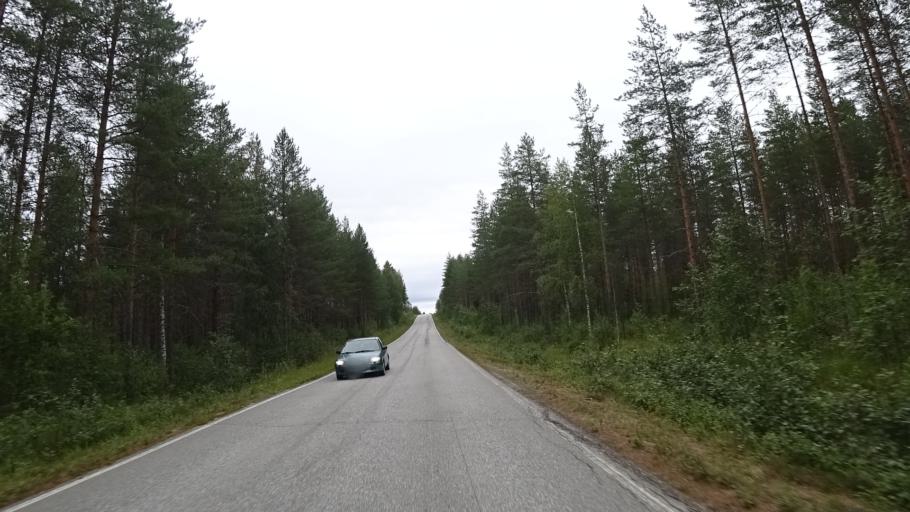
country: FI
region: North Karelia
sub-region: Pielisen Karjala
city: Lieksa
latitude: 63.3647
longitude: 30.2875
